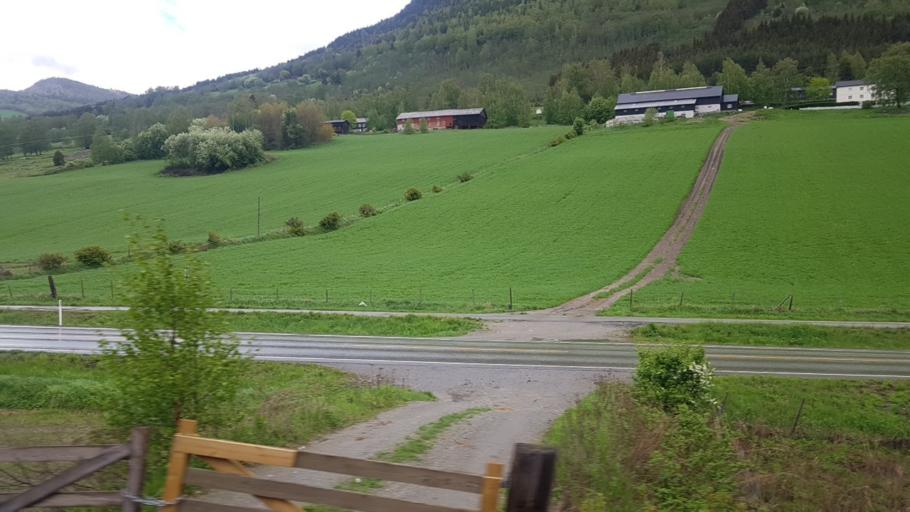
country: NO
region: Oppland
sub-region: Nord-Fron
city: Vinstra
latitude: 61.6638
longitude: 9.6738
